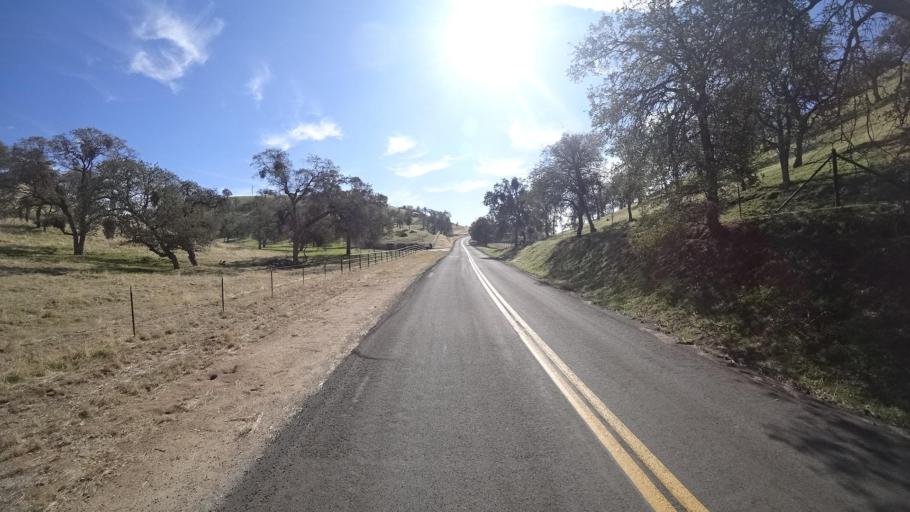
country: US
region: California
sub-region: Kern County
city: Oildale
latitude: 35.6481
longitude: -118.8405
